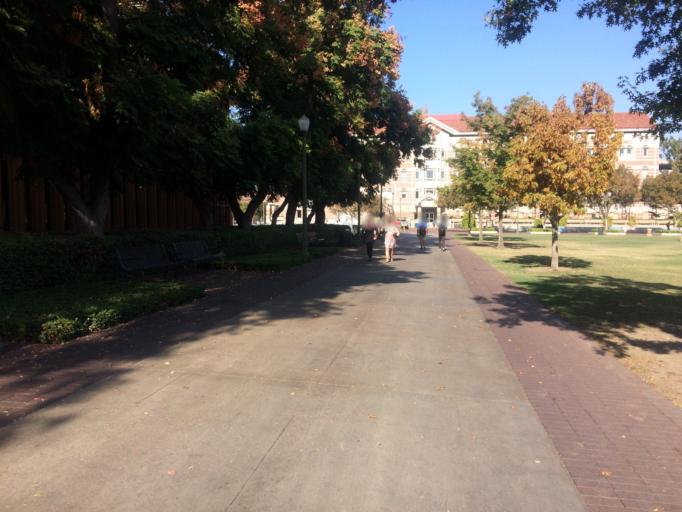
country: US
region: California
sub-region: Los Angeles County
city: Los Angeles
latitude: 34.0208
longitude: -118.2836
